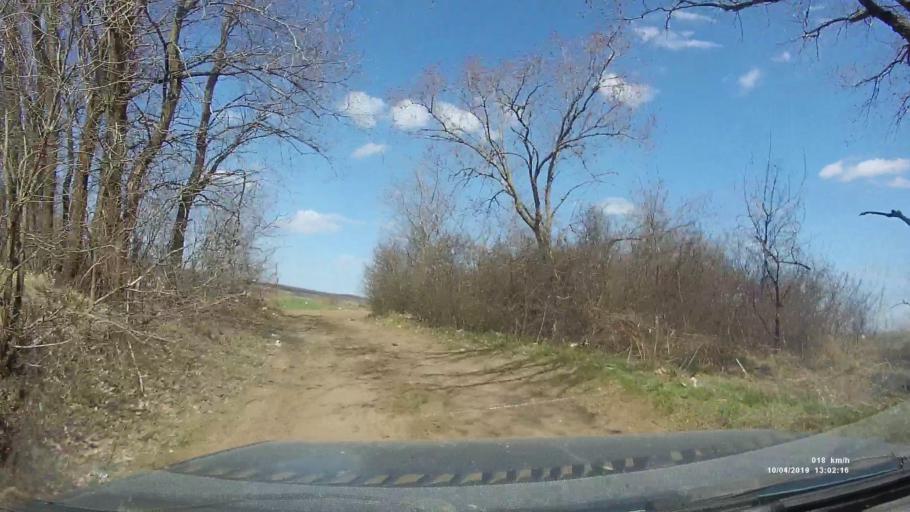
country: RU
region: Rostov
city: Masalovka
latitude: 48.3809
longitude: 40.2306
